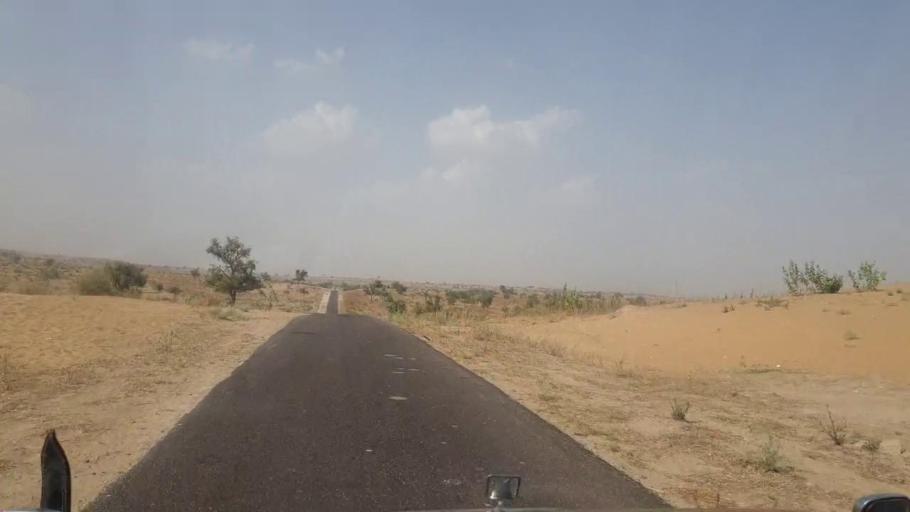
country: PK
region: Sindh
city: Islamkot
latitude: 25.1938
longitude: 70.2850
